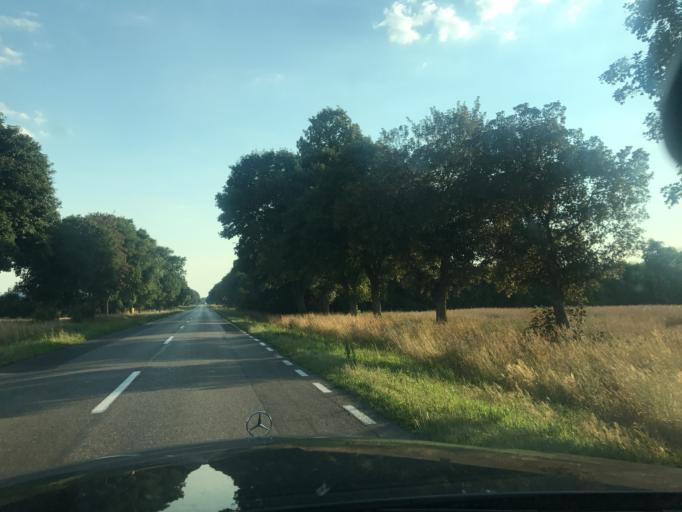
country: PL
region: Lublin Voivodeship
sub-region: Powiat bialski
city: Wisznice
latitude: 51.7609
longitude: 23.1824
